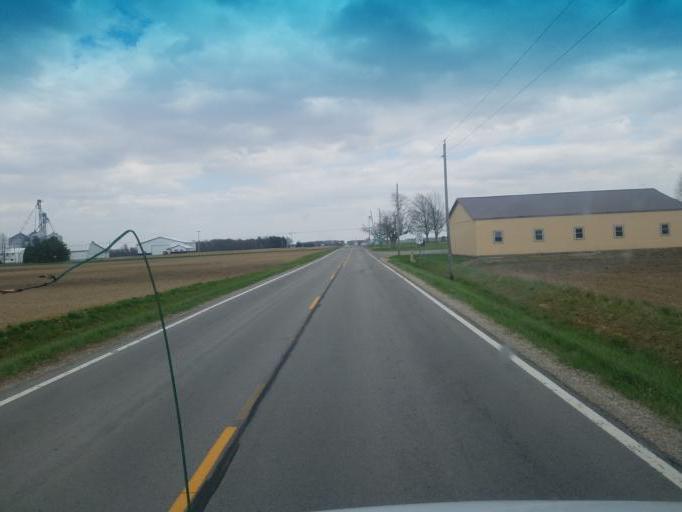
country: US
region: Ohio
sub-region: Crawford County
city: Bucyrus
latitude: 40.9502
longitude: -83.0186
